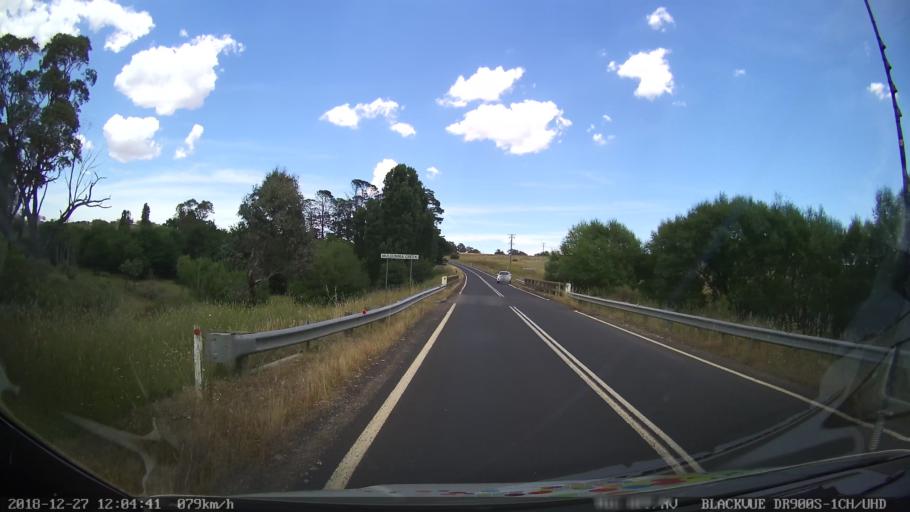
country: AU
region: New South Wales
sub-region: Blayney
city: Blayney
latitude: -33.7984
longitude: 149.3471
